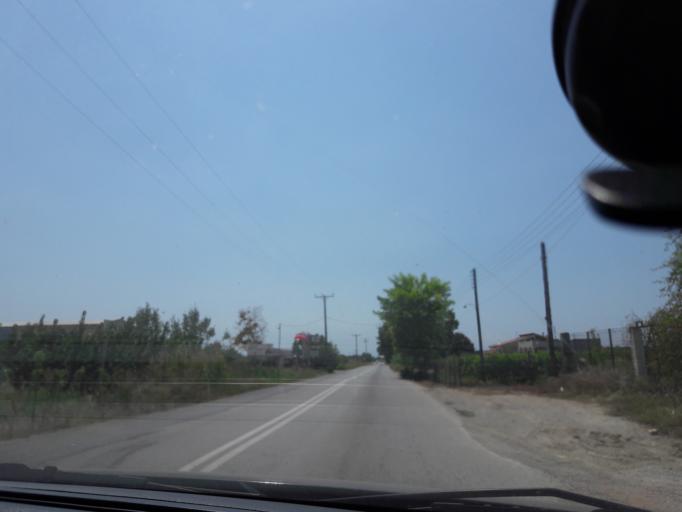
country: GR
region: Central Macedonia
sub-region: Nomos Chalkidikis
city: Nea Kallikrateia
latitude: 40.3357
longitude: 23.0637
